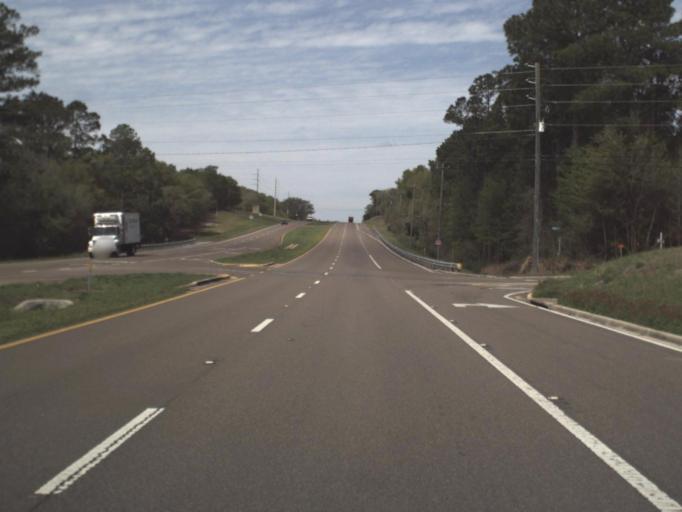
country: US
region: Florida
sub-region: Okaloosa County
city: Crestview
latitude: 30.7544
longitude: -86.5168
